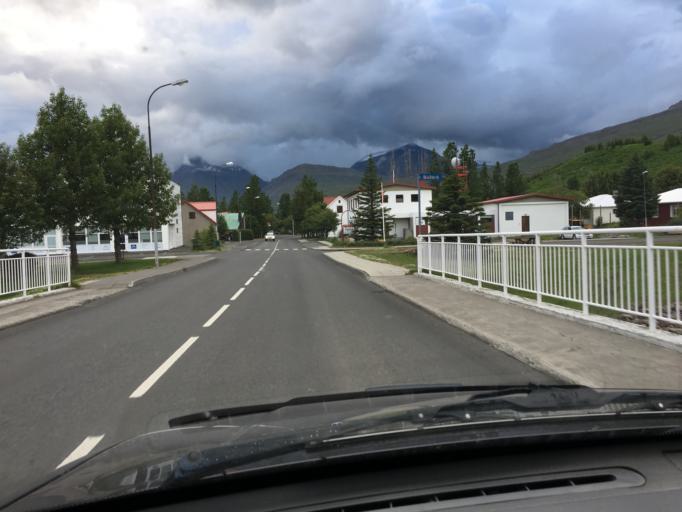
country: IS
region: East
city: Reydarfjoerdur
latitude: 65.0328
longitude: -14.2175
